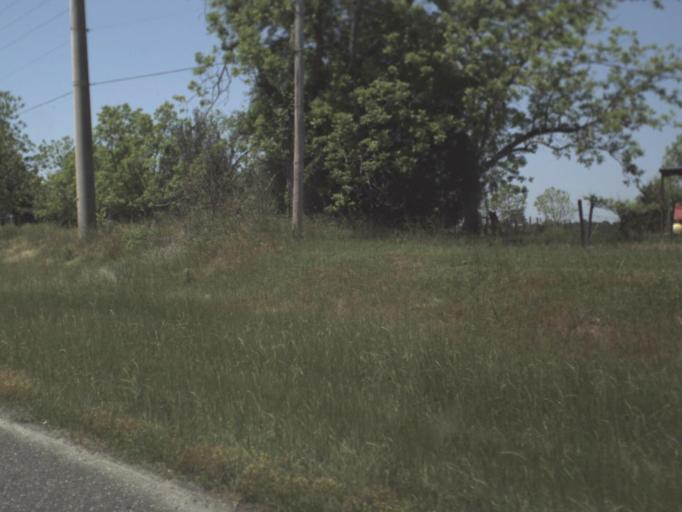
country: US
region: Florida
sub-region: Jefferson County
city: Monticello
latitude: 30.4876
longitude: -83.8837
